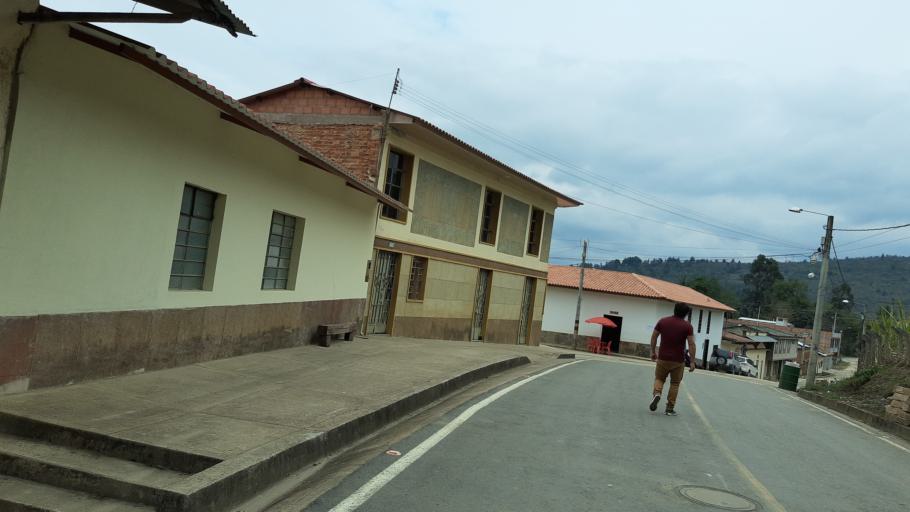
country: CO
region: Boyaca
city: Somondoco
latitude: 4.9703
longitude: -73.3797
